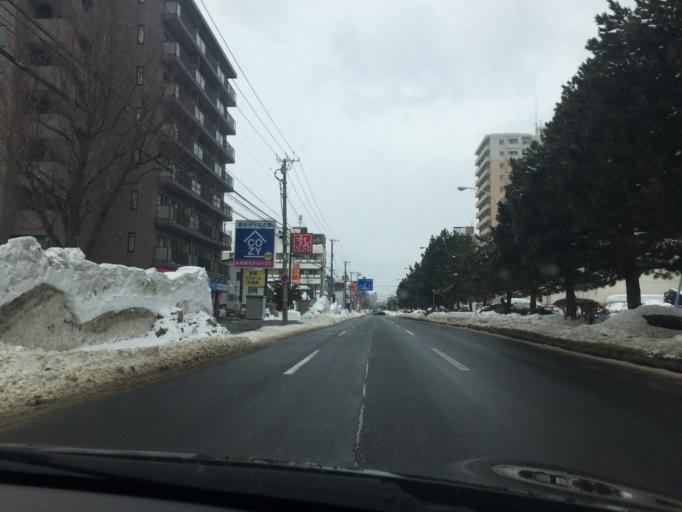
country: JP
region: Hokkaido
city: Sapporo
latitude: 43.0807
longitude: 141.3666
